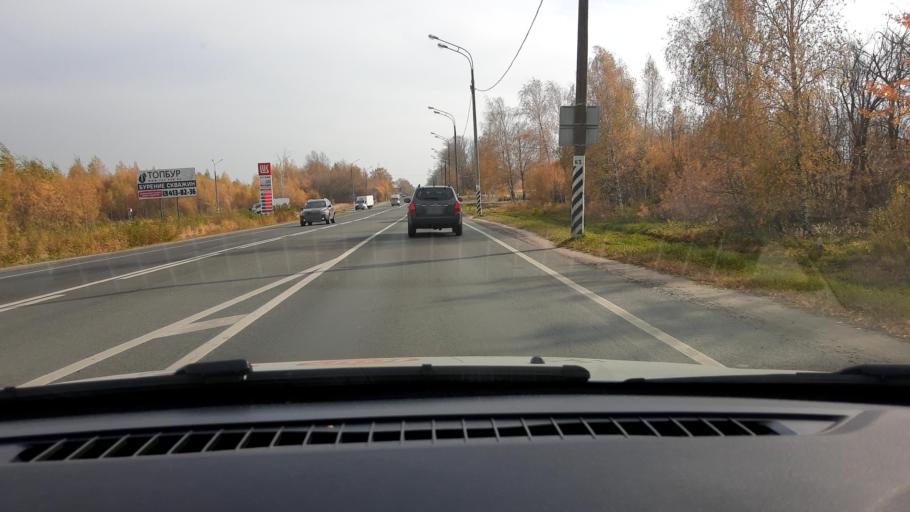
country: RU
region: Nizjnij Novgorod
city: Kstovo
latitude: 56.1436
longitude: 44.2219
